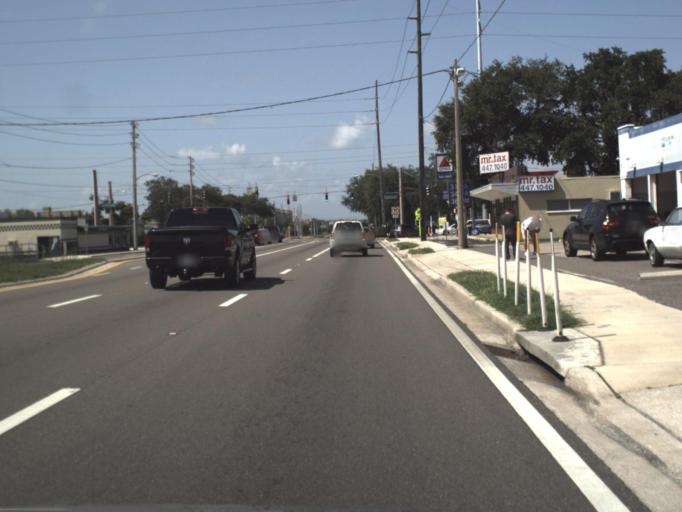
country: US
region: Florida
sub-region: Pinellas County
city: Clearwater
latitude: 27.9487
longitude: -82.7874
